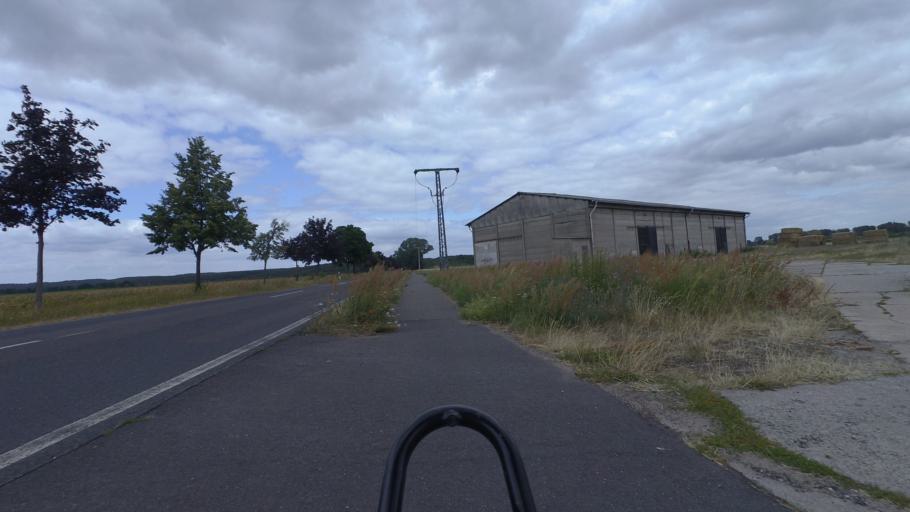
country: DE
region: Brandenburg
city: Trebbin
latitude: 52.2258
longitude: 13.1979
